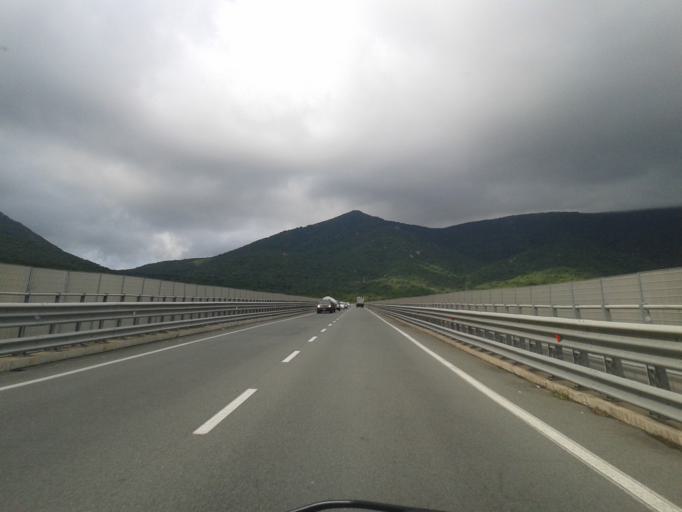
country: IT
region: Sardinia
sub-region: Provincia di Cagliari
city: Castiadas
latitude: 39.2279
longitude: 9.5005
